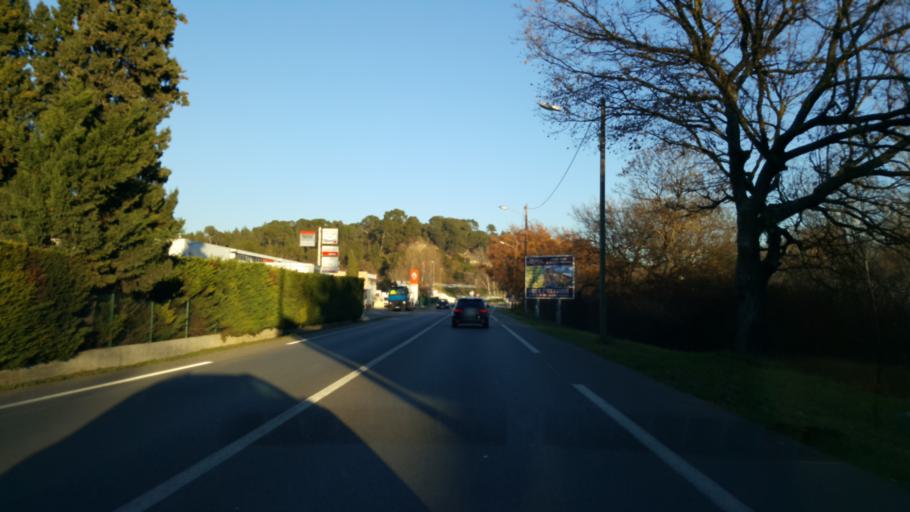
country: FR
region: Provence-Alpes-Cote d'Azur
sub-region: Departement des Bouches-du-Rhone
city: Meyreuil
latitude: 43.5121
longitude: 5.4767
